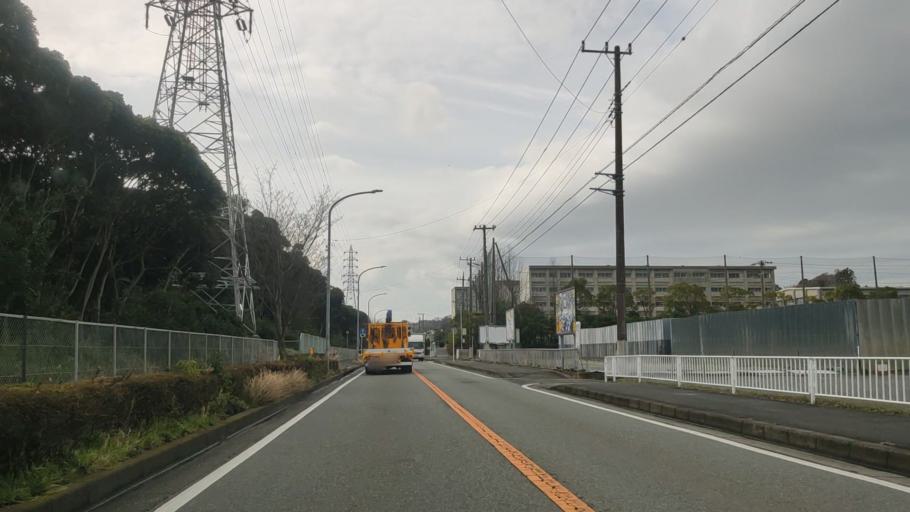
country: JP
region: Kanagawa
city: Fujisawa
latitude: 35.3759
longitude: 139.5249
